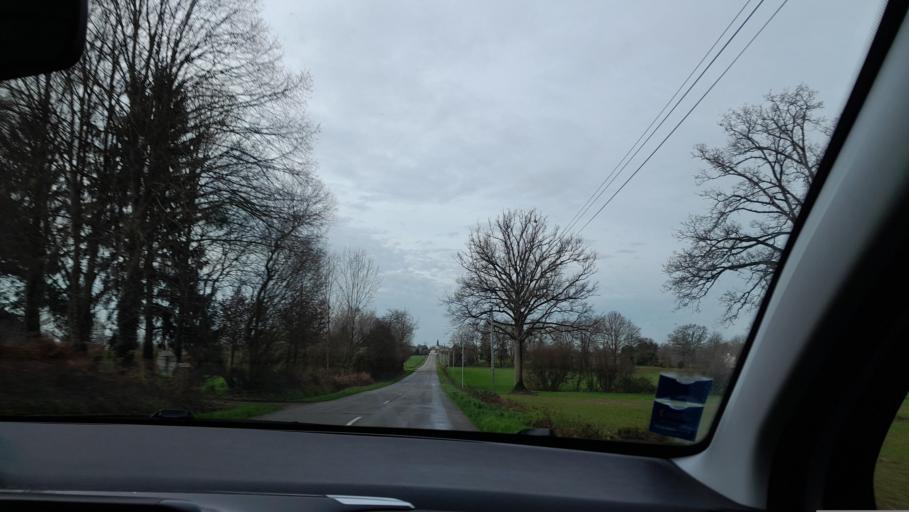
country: FR
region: Pays de la Loire
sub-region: Departement de la Mayenne
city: Ballots
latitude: 47.9477
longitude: -1.0746
